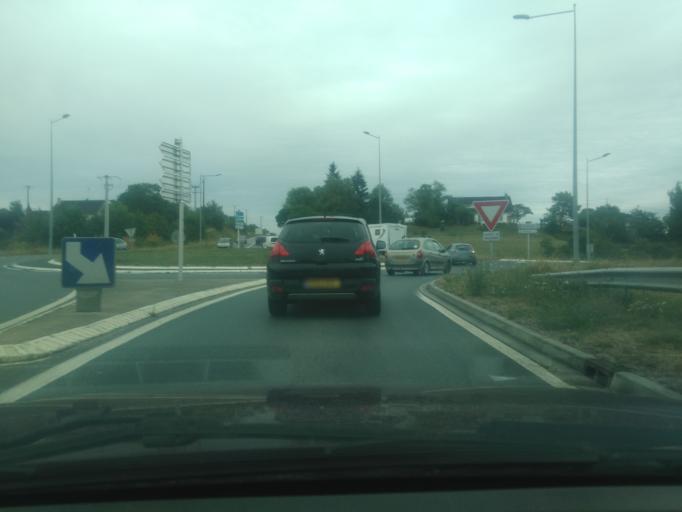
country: FR
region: Centre
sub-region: Departement de l'Indre
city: Saint-Gaultier
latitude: 46.6403
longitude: 1.3968
